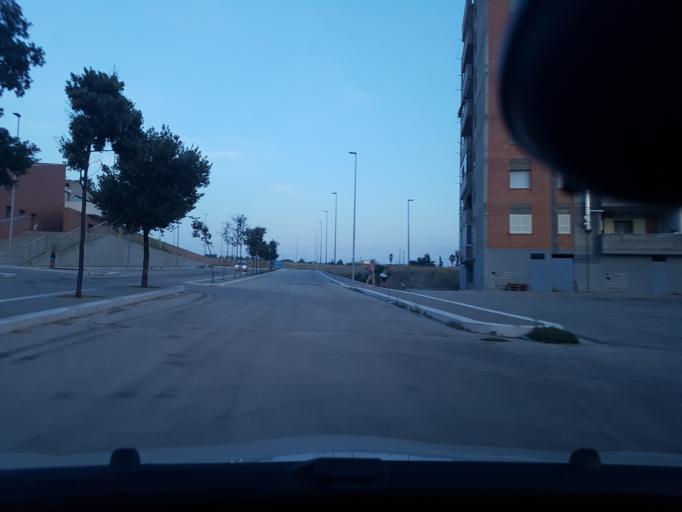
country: IT
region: Apulia
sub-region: Provincia di Foggia
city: Cerignola
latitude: 41.2597
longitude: 15.8759
